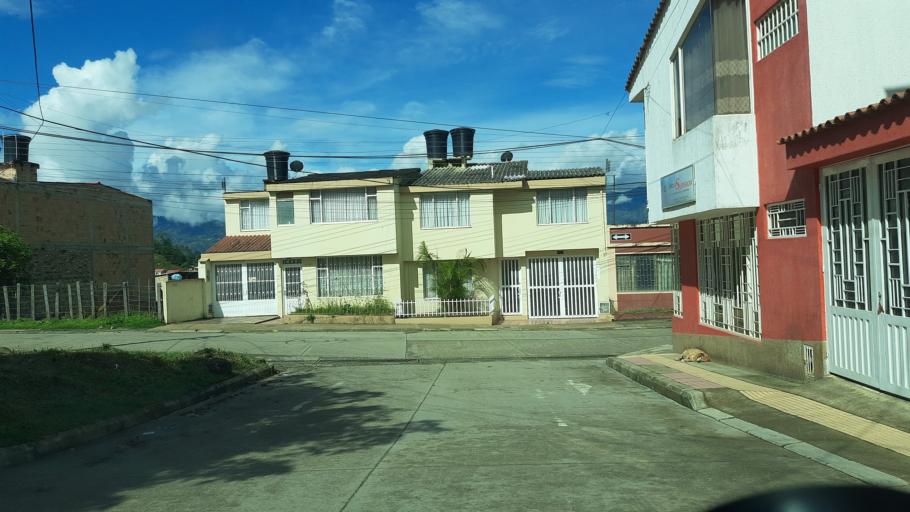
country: CO
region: Boyaca
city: Garagoa
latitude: 5.0790
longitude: -73.3625
